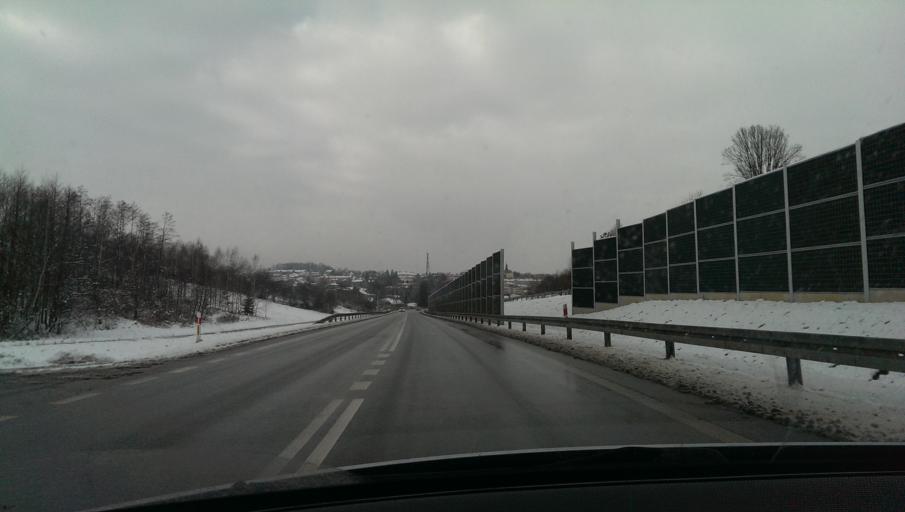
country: PL
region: Subcarpathian Voivodeship
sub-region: Powiat brzozowski
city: Brzozow
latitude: 49.6889
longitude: 22.0358
